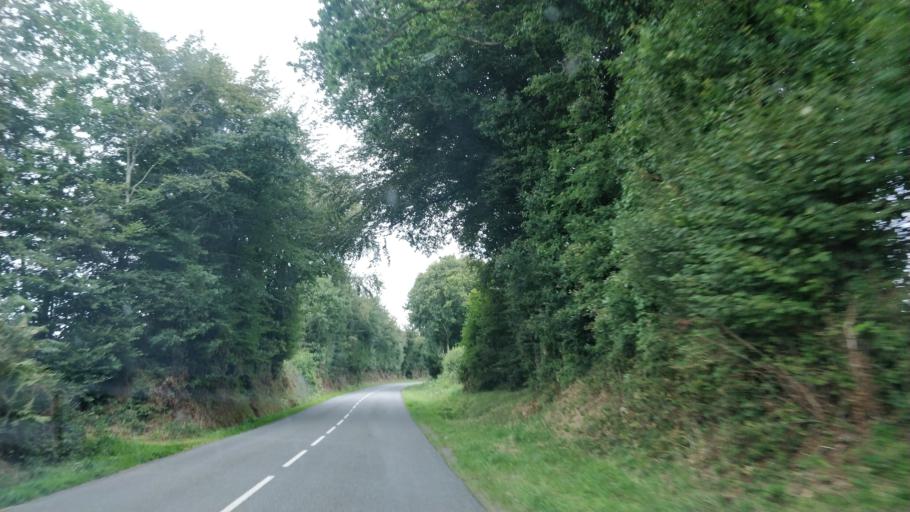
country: FR
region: Brittany
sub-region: Departement du Finistere
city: Loperhet
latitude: 48.3918
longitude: -4.3097
